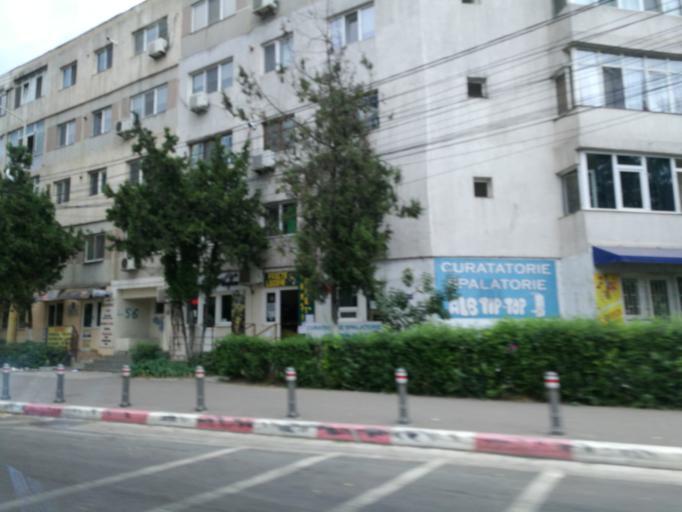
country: RO
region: Constanta
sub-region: Municipiul Constanta
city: Constanta
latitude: 44.1771
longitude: 28.6362
